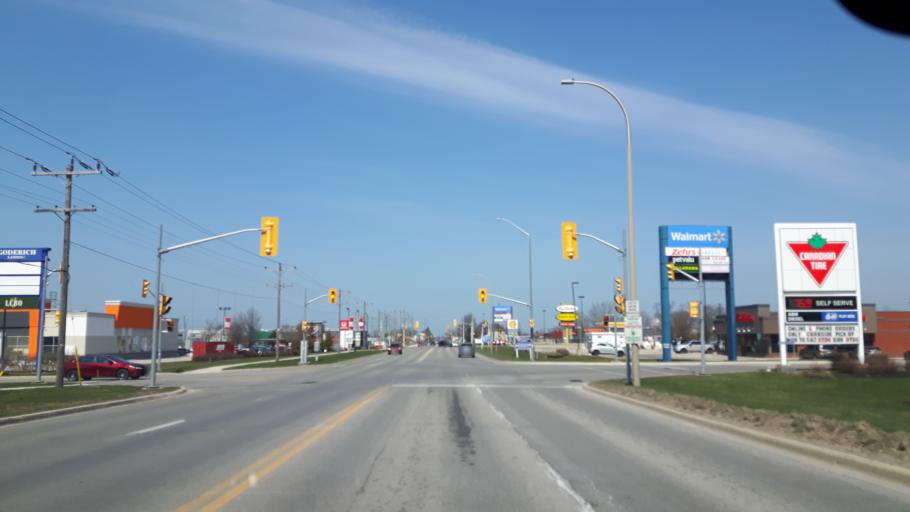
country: CA
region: Ontario
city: Goderich
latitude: 43.7292
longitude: -81.6879
